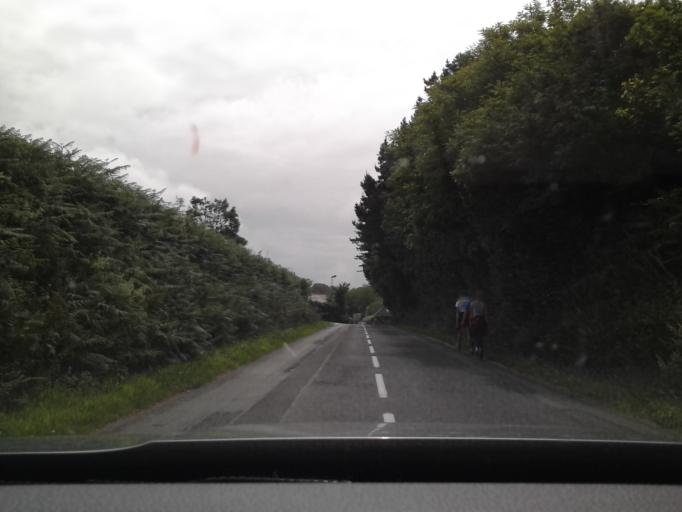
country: FR
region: Lower Normandy
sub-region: Departement de la Manche
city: Urville-Nacqueville
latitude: 49.6769
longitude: -1.7790
